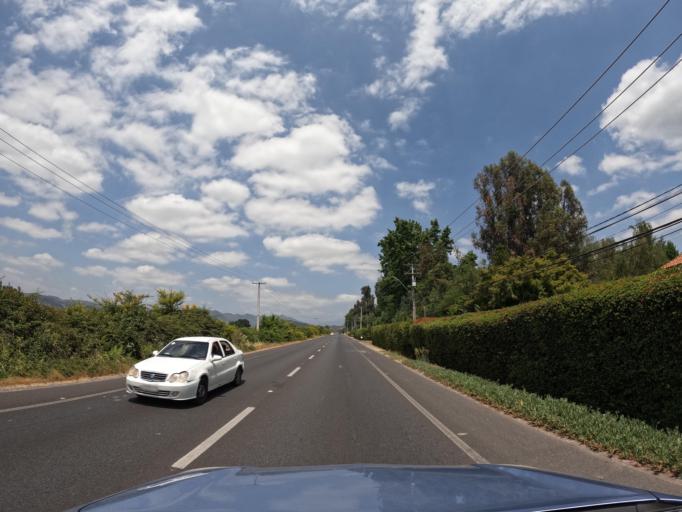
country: CL
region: Maule
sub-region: Provincia de Curico
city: Curico
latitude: -35.0195
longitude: -71.2086
